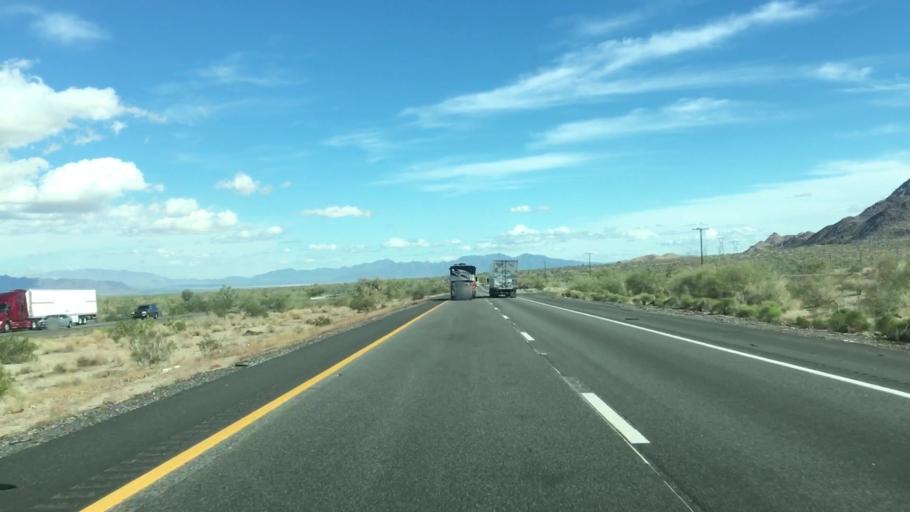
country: US
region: California
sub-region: Imperial County
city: Niland
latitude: 33.6897
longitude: -115.5093
